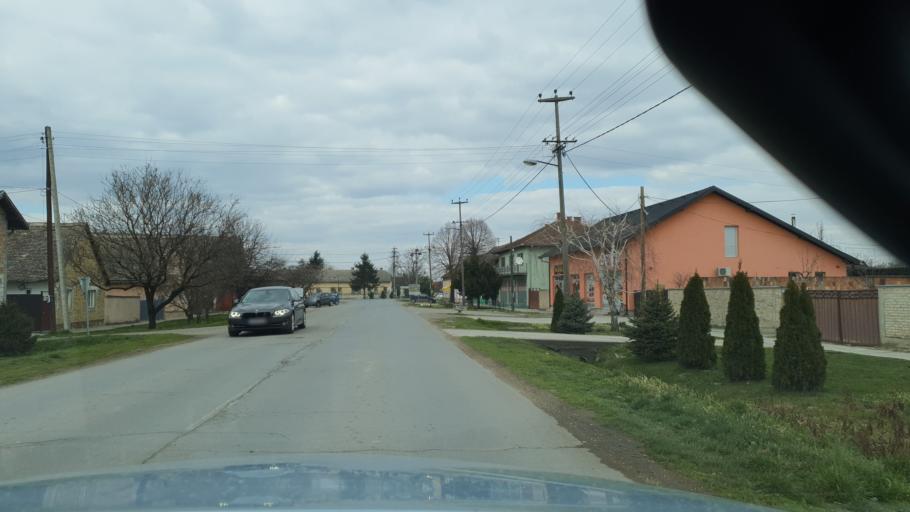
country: RS
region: Autonomna Pokrajina Vojvodina
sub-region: Juznobacki Okrug
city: Bac
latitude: 45.3938
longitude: 19.2372
